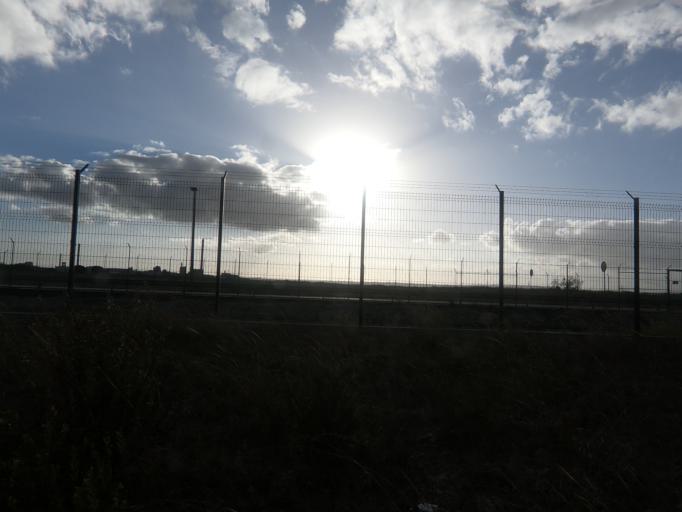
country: PT
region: Setubal
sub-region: Barreiro
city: Barreiro
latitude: 38.6786
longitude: -9.0554
